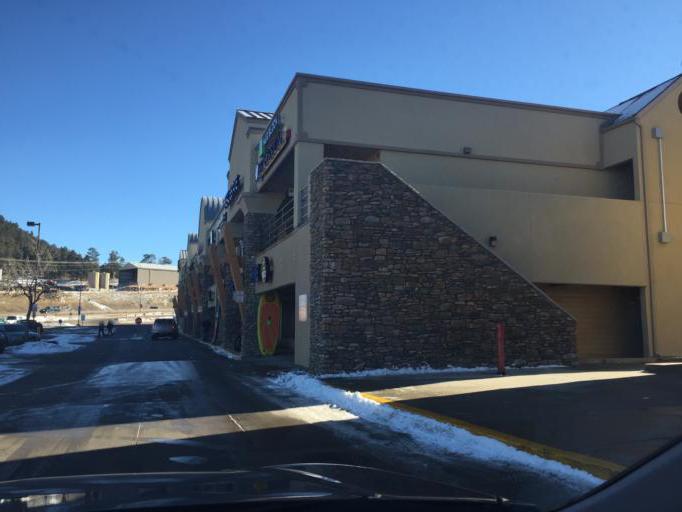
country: US
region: Colorado
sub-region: Jefferson County
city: Evergreen
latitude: 39.5192
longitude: -105.3068
